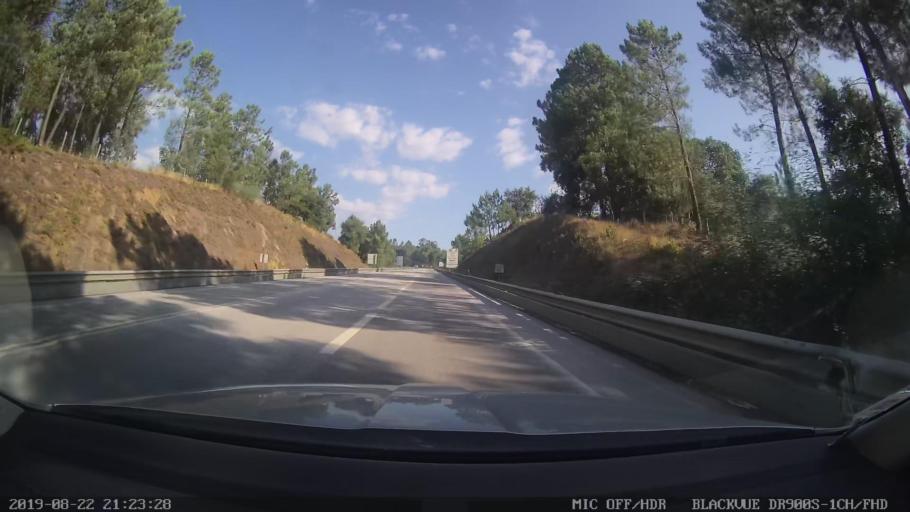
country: PT
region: Castelo Branco
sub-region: Serta
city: Serta
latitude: 39.8313
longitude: -8.1096
